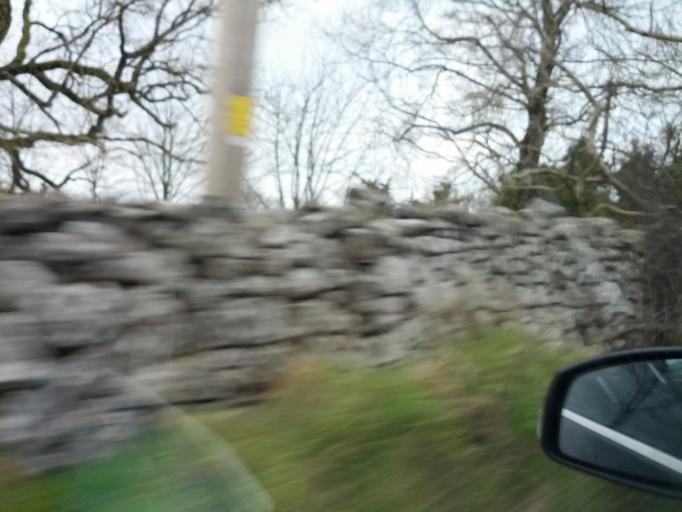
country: IE
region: Connaught
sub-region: County Galway
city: Oranmore
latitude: 53.2554
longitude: -8.8372
